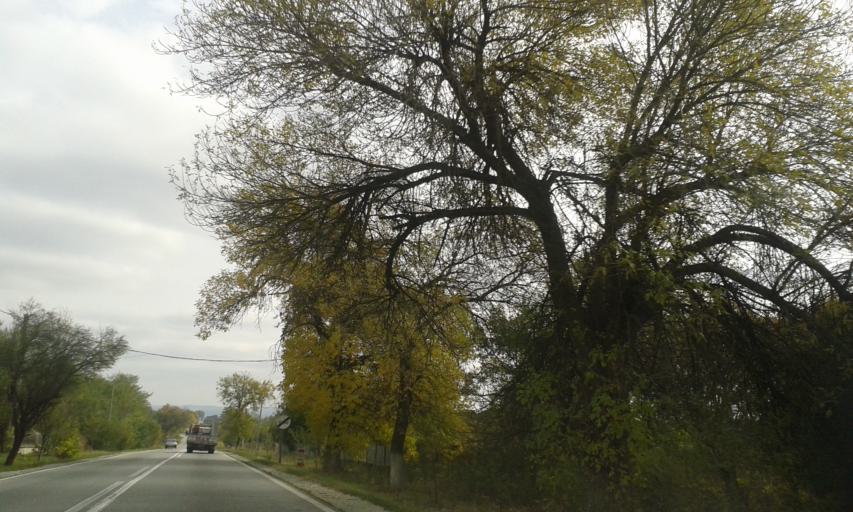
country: RO
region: Gorj
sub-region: Comuna Scoarta
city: Scoarta
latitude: 45.0314
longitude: 23.4150
